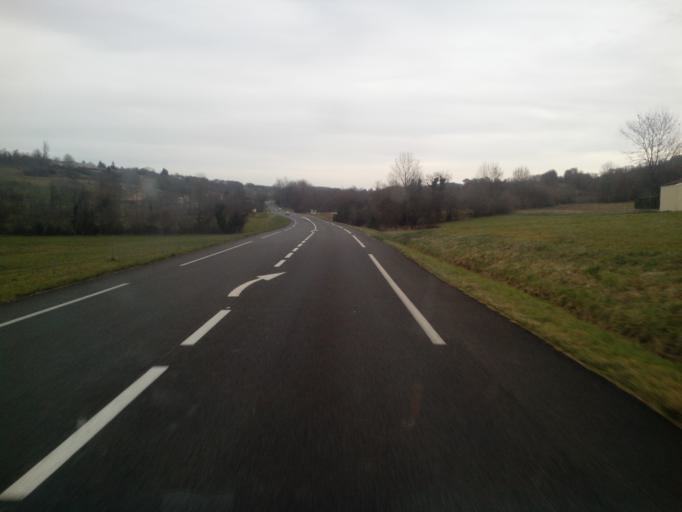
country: FR
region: Midi-Pyrenees
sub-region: Departement de l'Ariege
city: Foix
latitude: 43.0067
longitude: 1.4903
